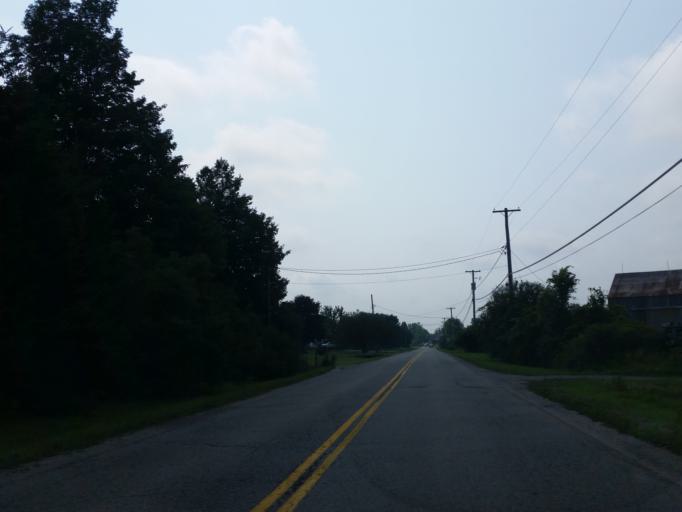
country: CA
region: Ontario
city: Brockville
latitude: 44.6257
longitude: -75.7537
